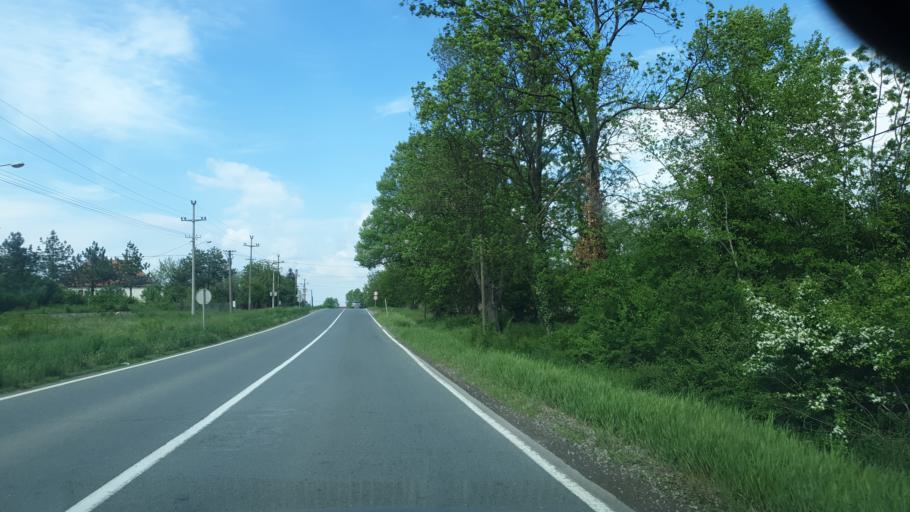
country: RS
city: Stubline
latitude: 44.5967
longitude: 20.1459
